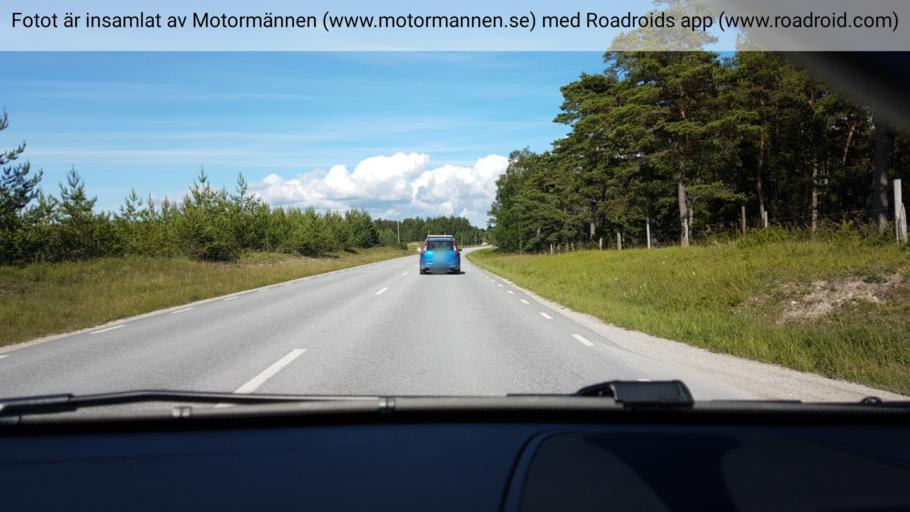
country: SE
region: Gotland
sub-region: Gotland
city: Slite
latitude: 57.7466
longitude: 18.6947
